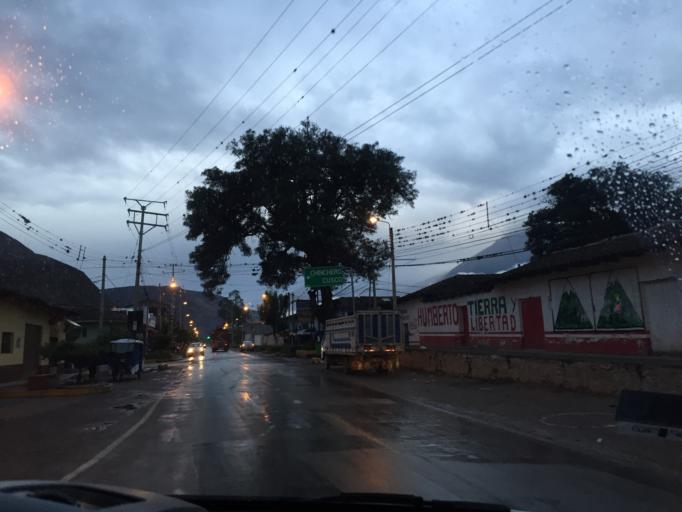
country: PE
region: Cusco
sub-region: Provincia de Urubamba
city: Urubamba
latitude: -13.3106
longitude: -72.1108
